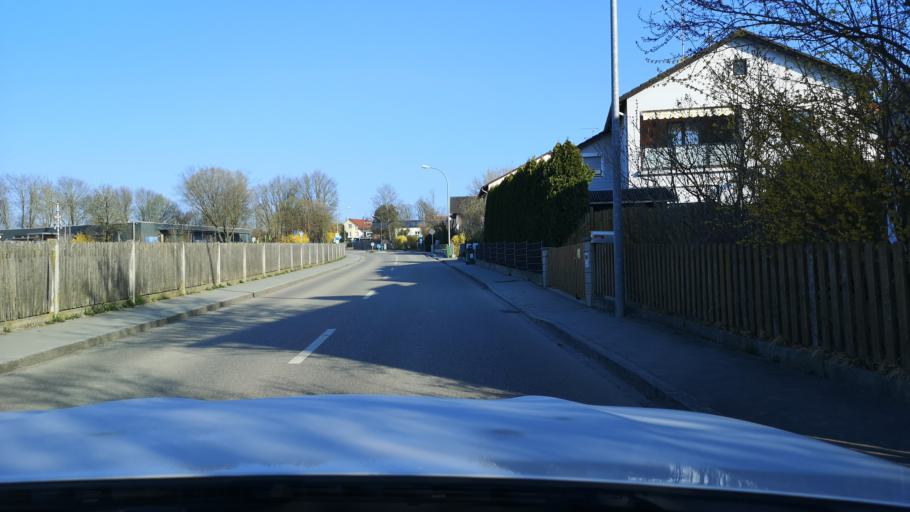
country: DE
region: Bavaria
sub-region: Upper Bavaria
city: Markt Schwaben
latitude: 48.1976
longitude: 11.8593
